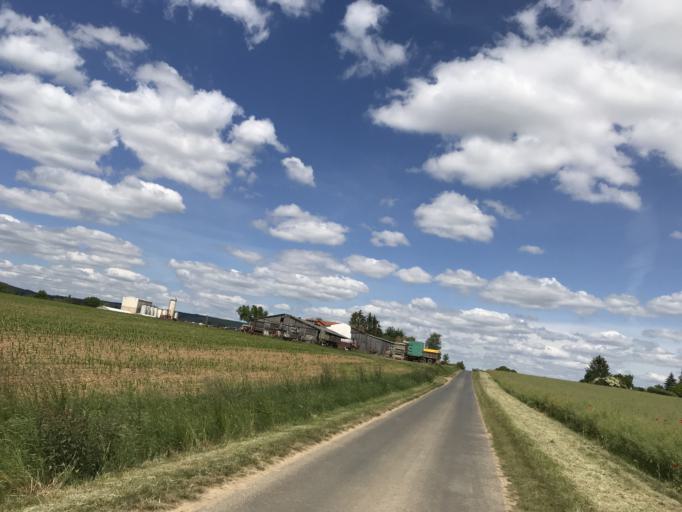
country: DE
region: Hesse
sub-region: Regierungsbezirk Darmstadt
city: Ober-Morlen
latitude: 50.3967
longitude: 8.6727
